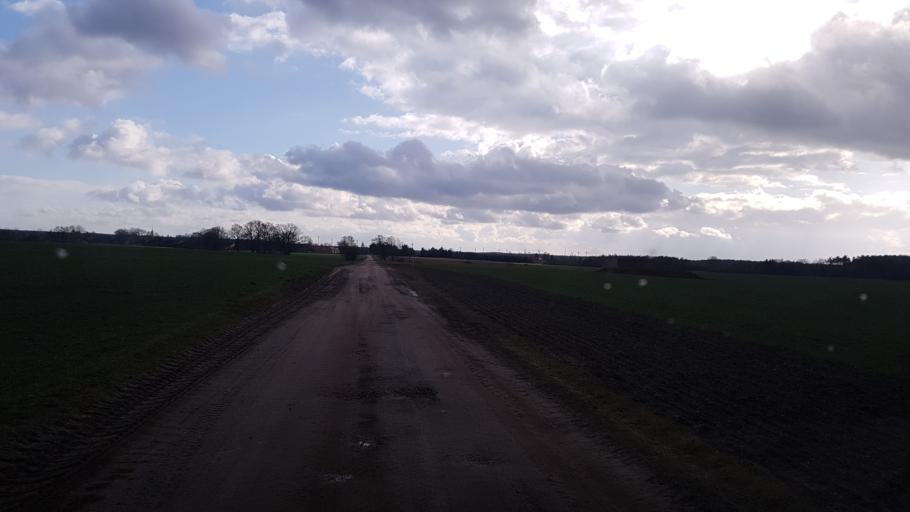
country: DE
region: Brandenburg
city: Sallgast
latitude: 51.6186
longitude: 13.8559
